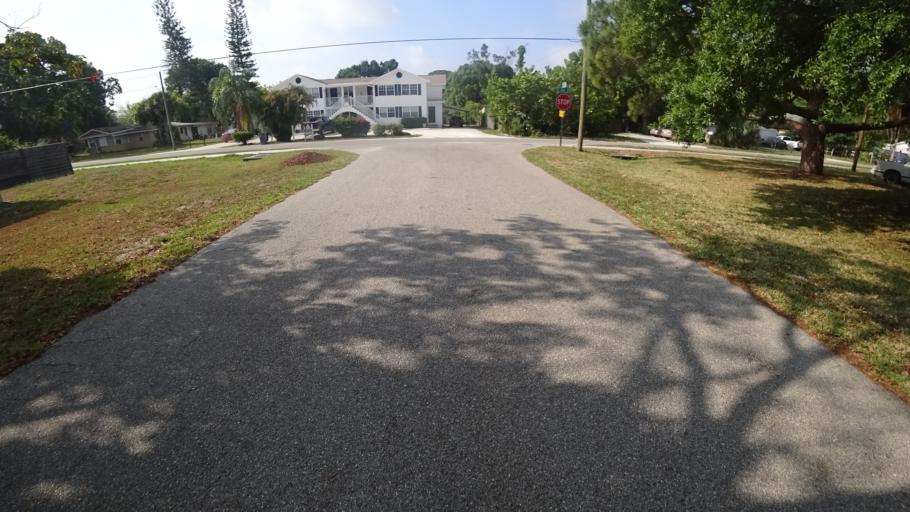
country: US
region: Florida
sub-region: Manatee County
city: West Bradenton
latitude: 27.5014
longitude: -82.6053
